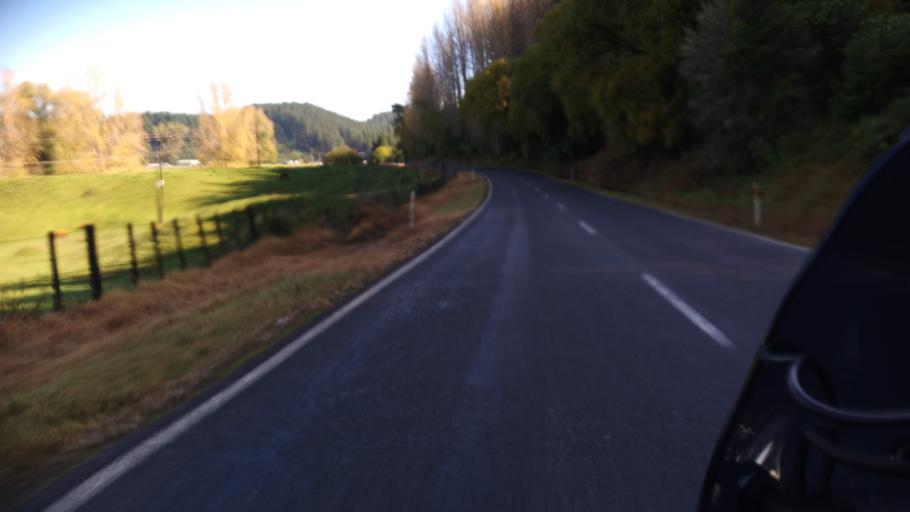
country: NZ
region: Hawke's Bay
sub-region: Wairoa District
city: Wairoa
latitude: -38.9243
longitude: 177.2715
